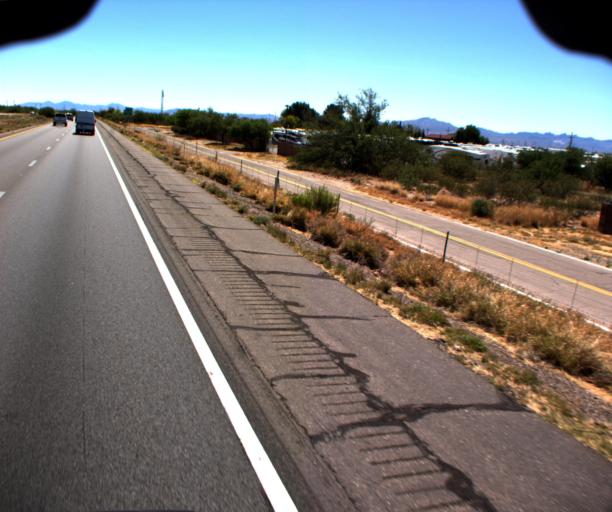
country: US
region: Arizona
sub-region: Pima County
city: Vail
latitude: 32.0940
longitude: -110.8256
